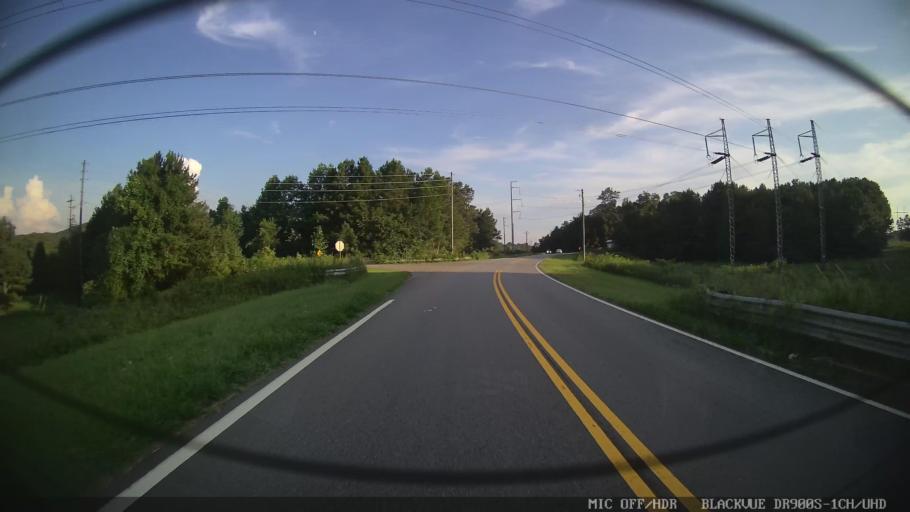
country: US
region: Georgia
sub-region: Bartow County
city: Cartersville
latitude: 34.2096
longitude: -84.7804
